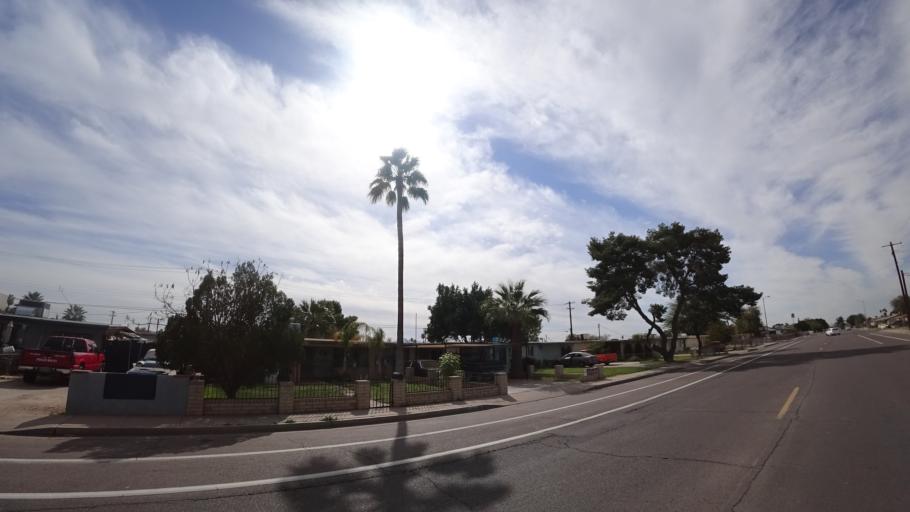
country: US
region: Arizona
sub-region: Maricopa County
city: Phoenix
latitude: 33.4732
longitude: -112.1462
